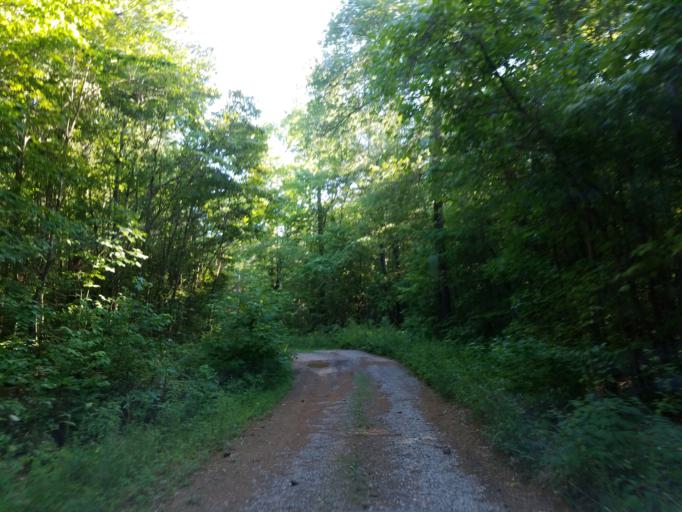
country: US
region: Georgia
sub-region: Gordon County
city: Calhoun
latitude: 34.6169
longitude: -85.0449
